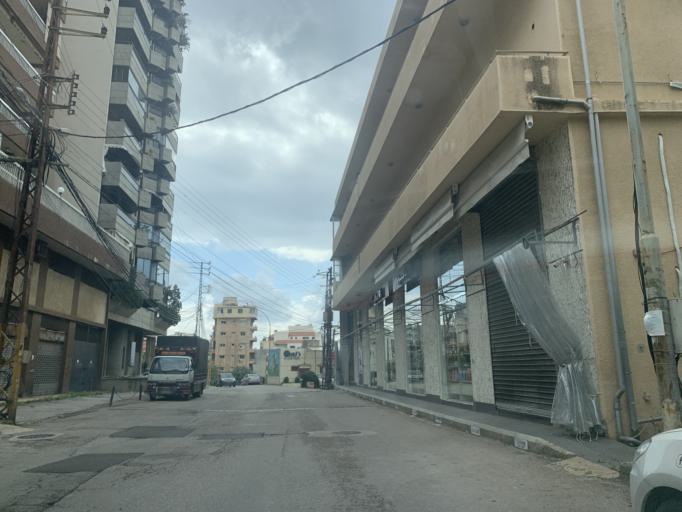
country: LB
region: Mont-Liban
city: Djounie
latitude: 33.9858
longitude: 35.6426
